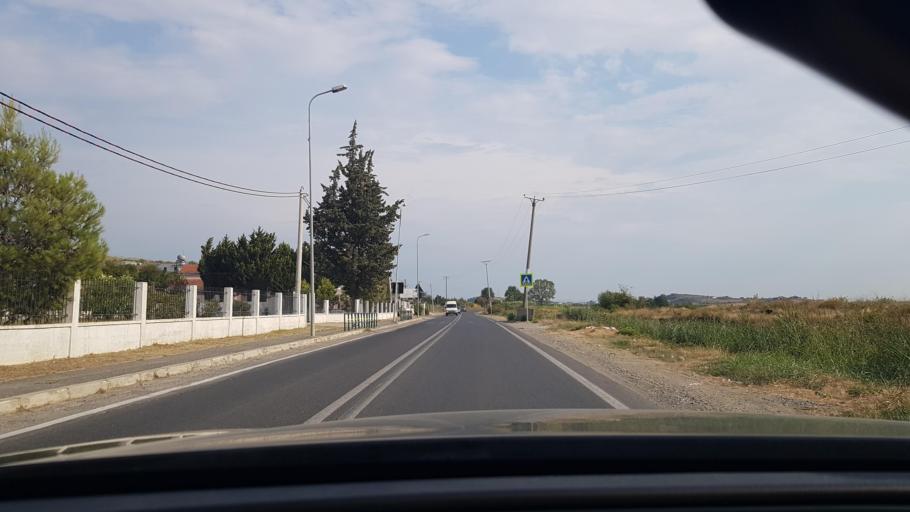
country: AL
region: Durres
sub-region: Rrethi i Durresit
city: Manze
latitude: 41.4617
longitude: 19.5640
